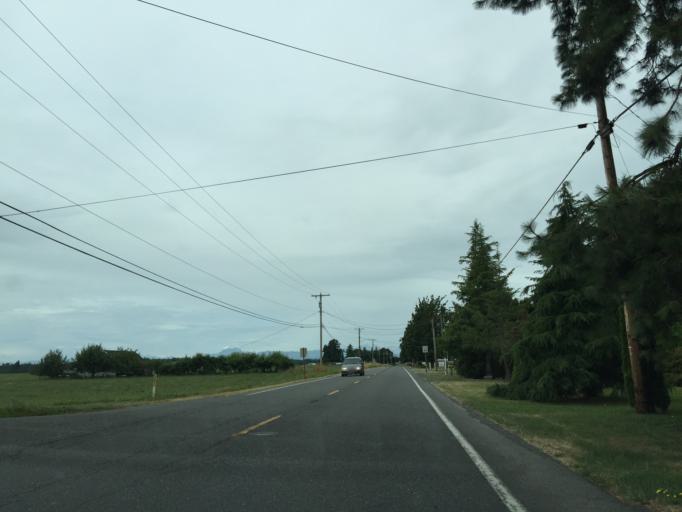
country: US
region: Washington
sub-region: Whatcom County
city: Nooksack
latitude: 48.9346
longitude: -122.3217
